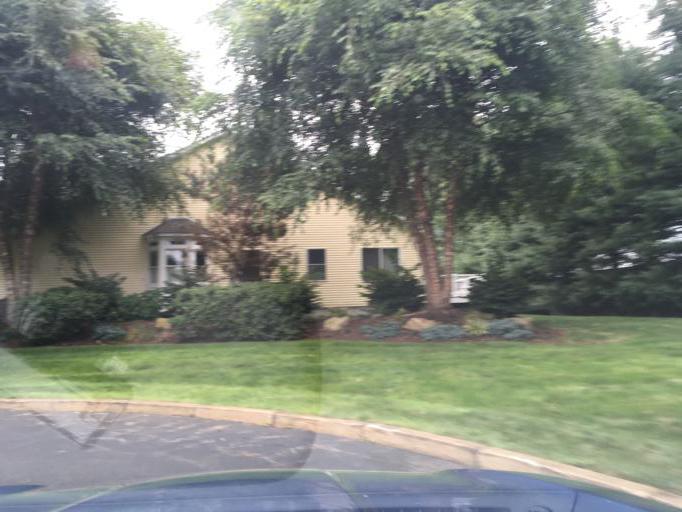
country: US
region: Rhode Island
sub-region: Kent County
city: West Warwick
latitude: 41.6598
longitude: -71.5075
